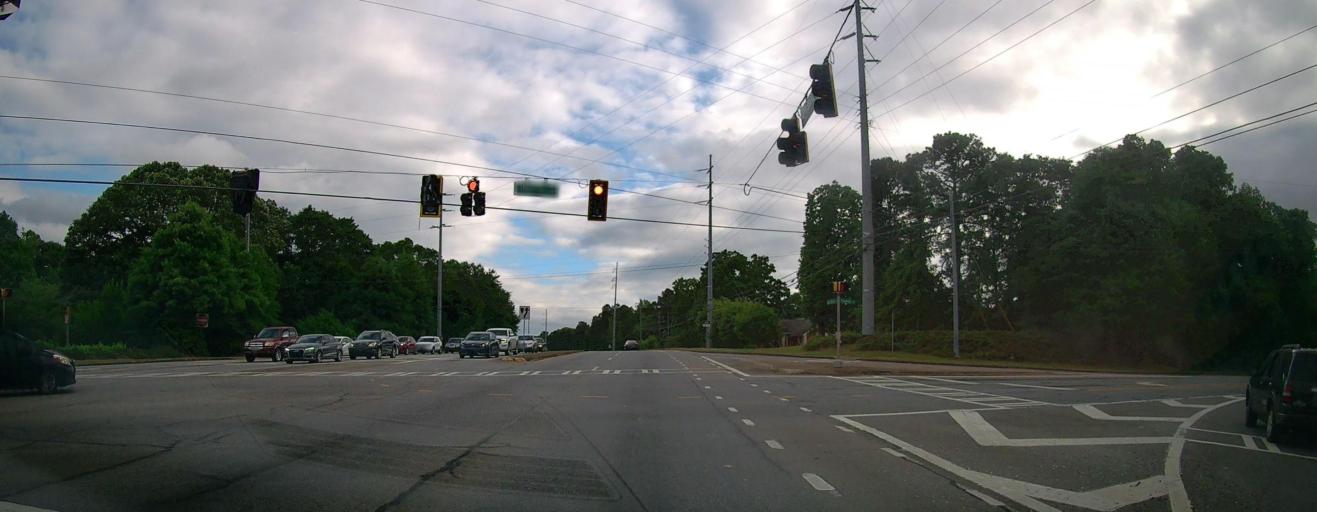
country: US
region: Georgia
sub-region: Clarke County
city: Country Club Estates
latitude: 33.9341
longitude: -83.4371
